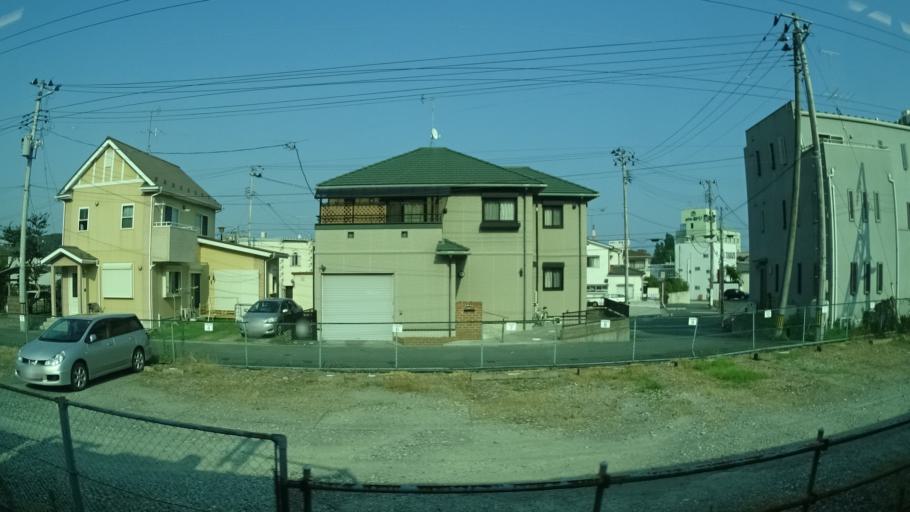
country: JP
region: Ibaraki
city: Kitaibaraki
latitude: 36.9192
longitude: 140.7966
